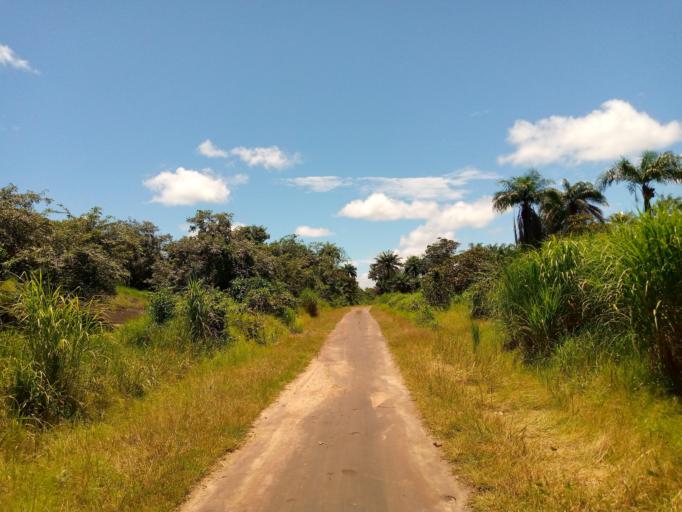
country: SL
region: Northern Province
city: Binkolo
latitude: 9.0943
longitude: -12.1421
